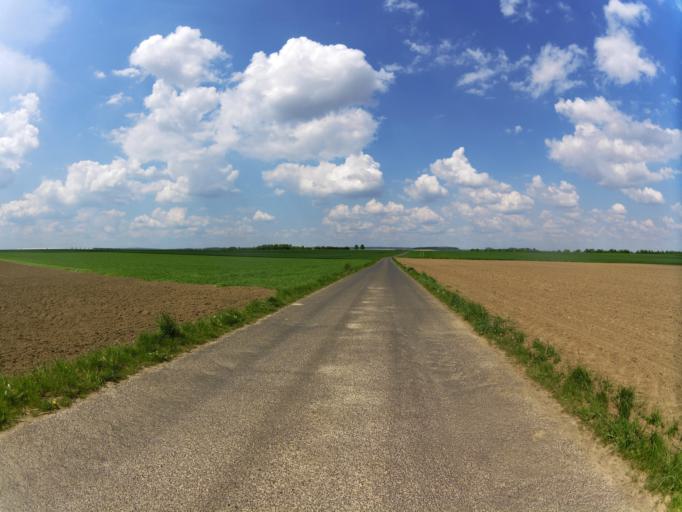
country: DE
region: Bavaria
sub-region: Regierungsbezirk Unterfranken
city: Giebelstadt
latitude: 49.6353
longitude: 9.9271
